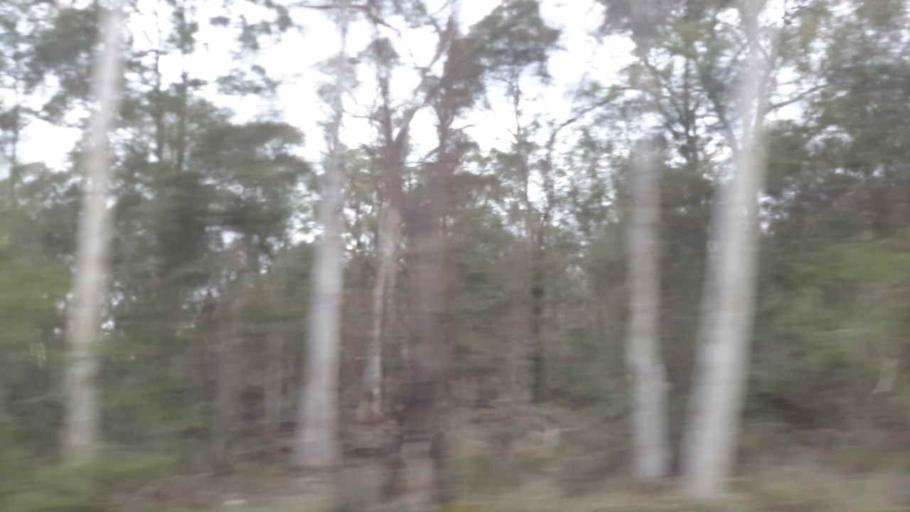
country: AU
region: New South Wales
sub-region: Hawkesbury
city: Richmond
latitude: -33.6660
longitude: 150.7574
